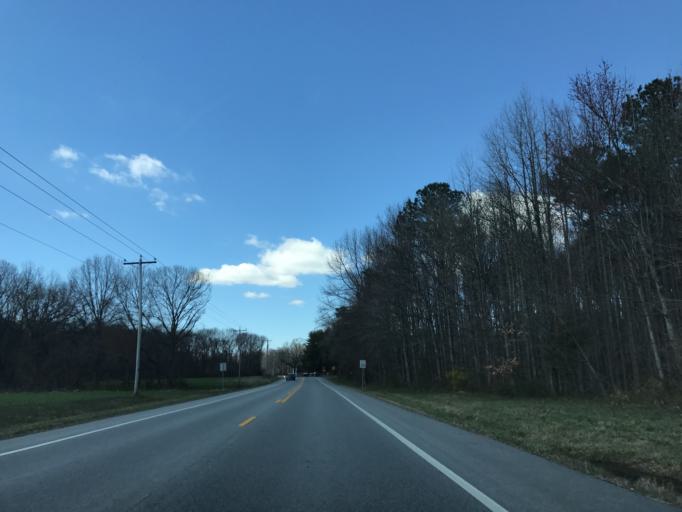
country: US
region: Maryland
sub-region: Queen Anne's County
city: Kingstown
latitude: 39.1155
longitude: -75.9141
